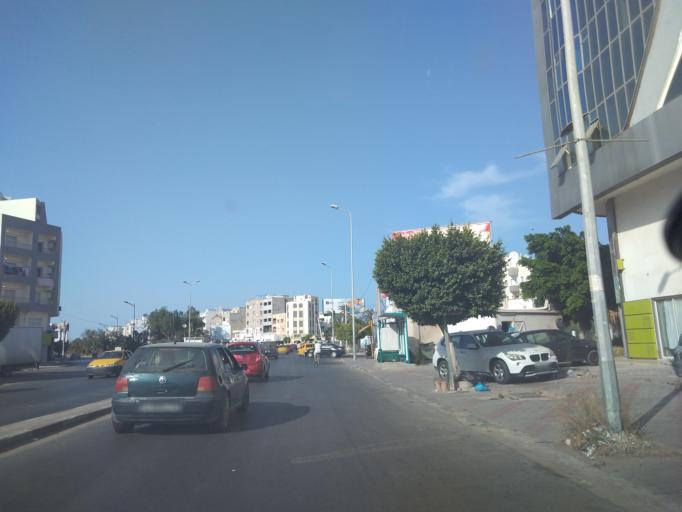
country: TN
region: Safaqis
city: Sfax
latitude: 34.7437
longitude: 10.7642
